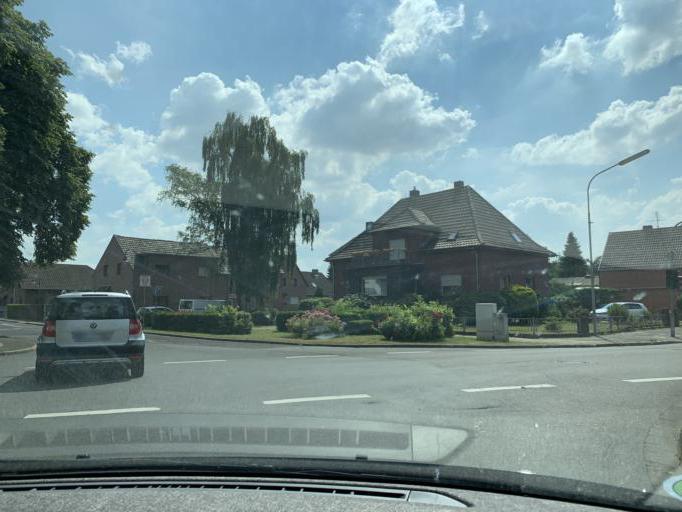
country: DE
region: North Rhine-Westphalia
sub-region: Regierungsbezirk Koln
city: Elsdorf
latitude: 50.9261
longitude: 6.5909
